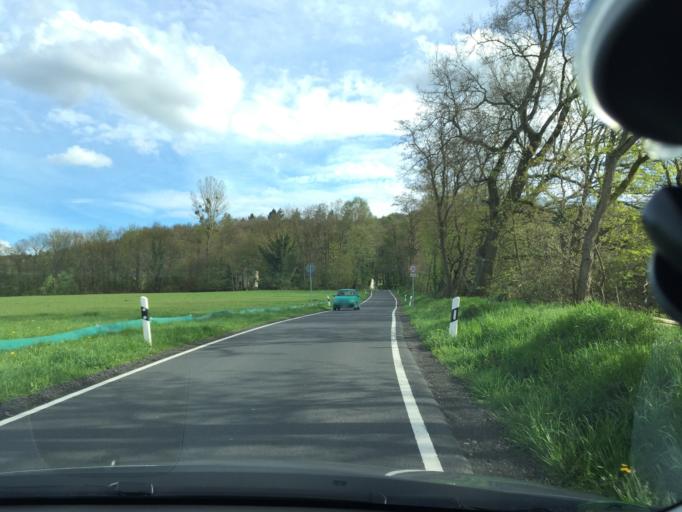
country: DE
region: Bavaria
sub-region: Regierungsbezirk Unterfranken
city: Goldbach
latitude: 49.9824
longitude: 9.1765
